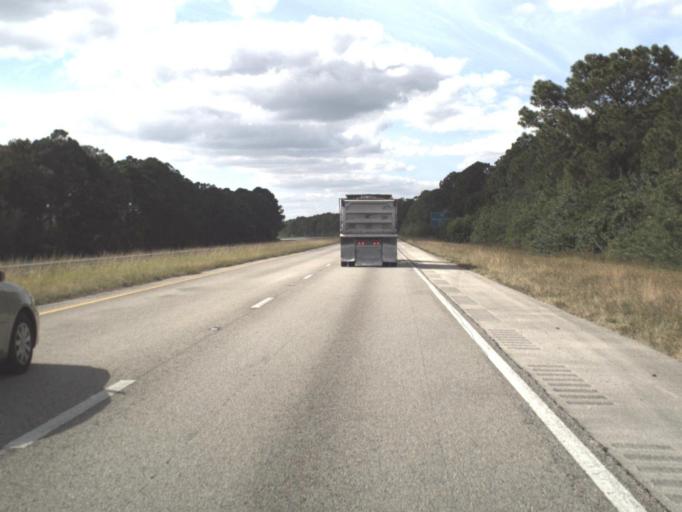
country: US
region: Florida
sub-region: Brevard County
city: Sharpes
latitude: 28.4109
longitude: -80.8040
